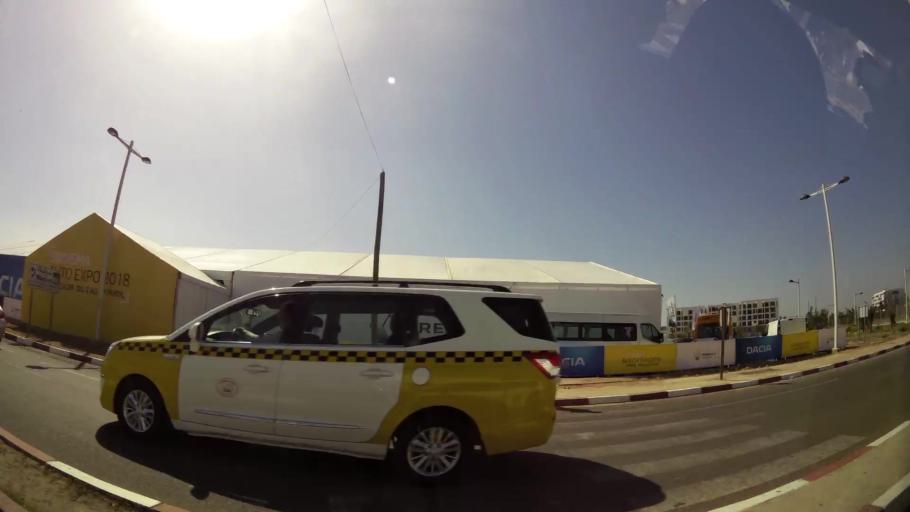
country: MA
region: Souss-Massa-Draa
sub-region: Agadir-Ida-ou-Tnan
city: Agadir
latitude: 30.3967
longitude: -9.5820
